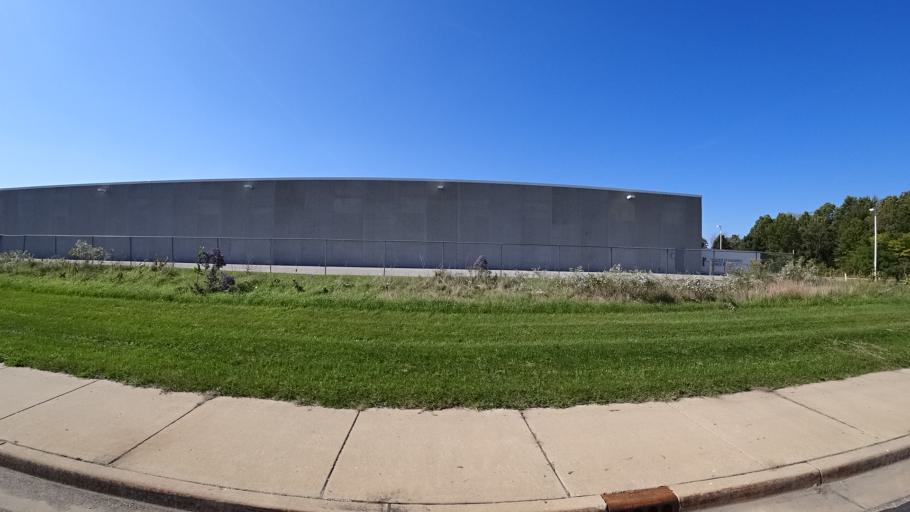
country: US
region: Indiana
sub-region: LaPorte County
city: Michigan City
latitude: 41.6760
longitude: -86.8887
